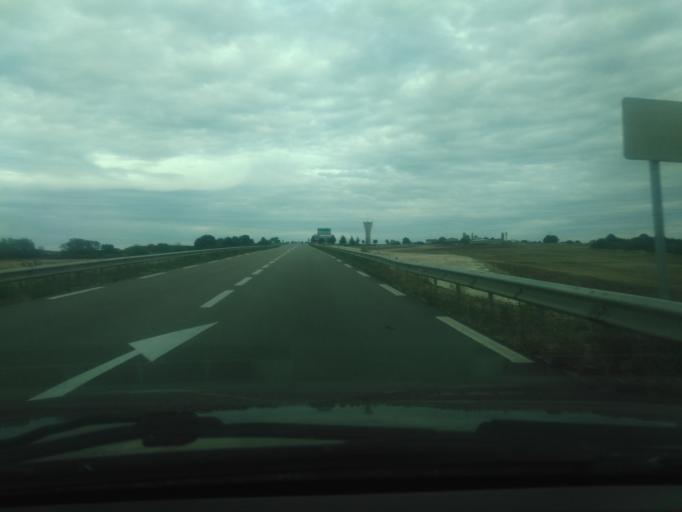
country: FR
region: Bourgogne
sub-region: Departement de la Nievre
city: Saint-Pierre-le-Moutier
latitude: 46.8025
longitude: 3.1130
